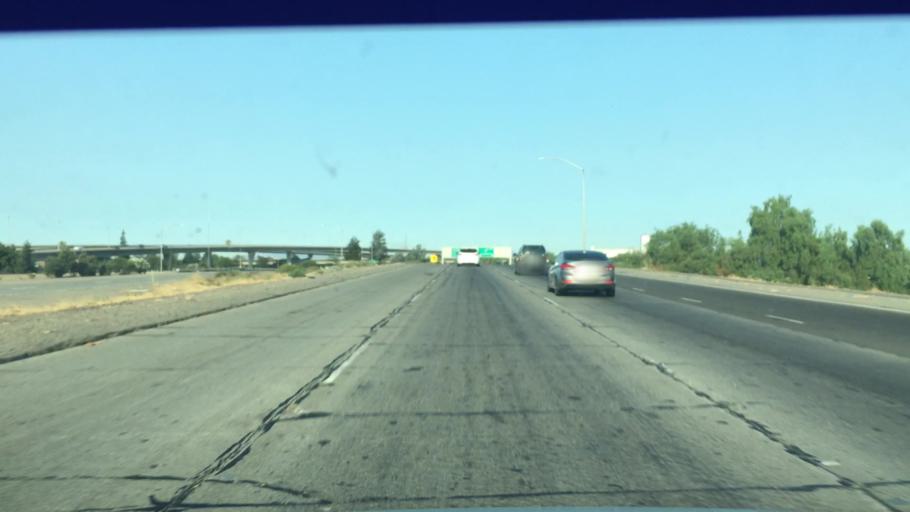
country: US
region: California
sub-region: San Joaquin County
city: Stockton
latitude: 37.9498
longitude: -121.2942
